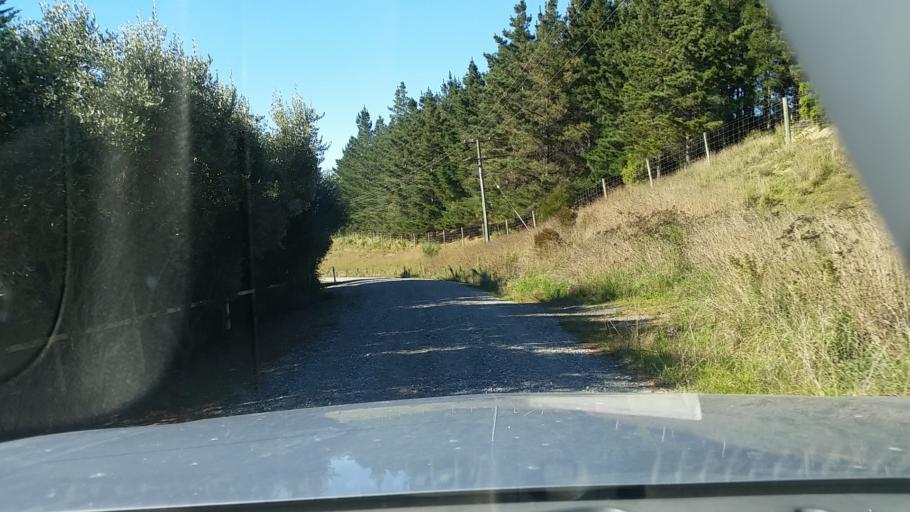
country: NZ
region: Marlborough
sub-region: Marlborough District
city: Blenheim
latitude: -41.6657
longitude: 174.1555
